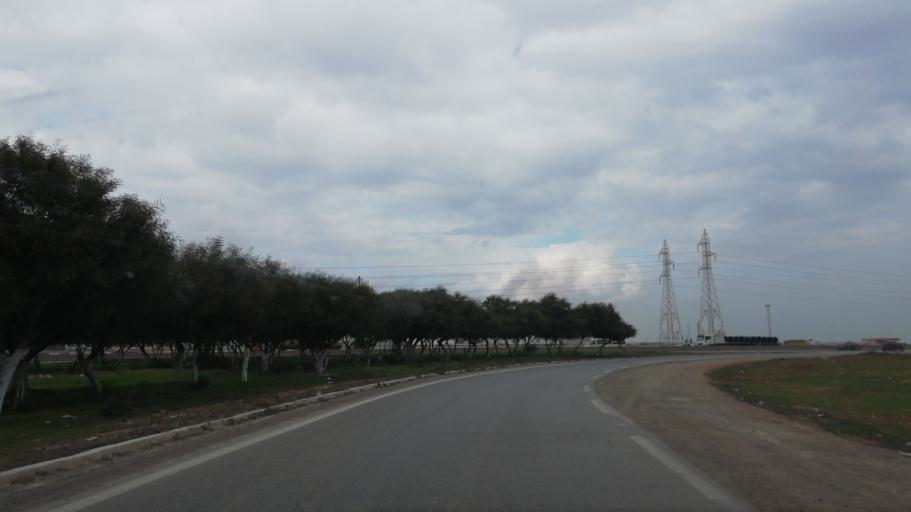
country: DZ
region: Oran
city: Ain el Bya
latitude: 35.7987
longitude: -0.3442
